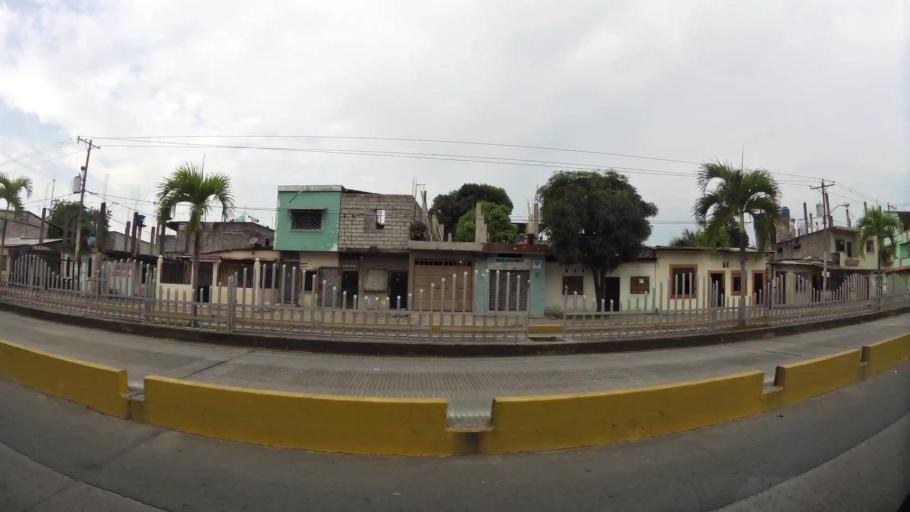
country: EC
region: Guayas
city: Guayaquil
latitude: -2.2558
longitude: -79.8794
